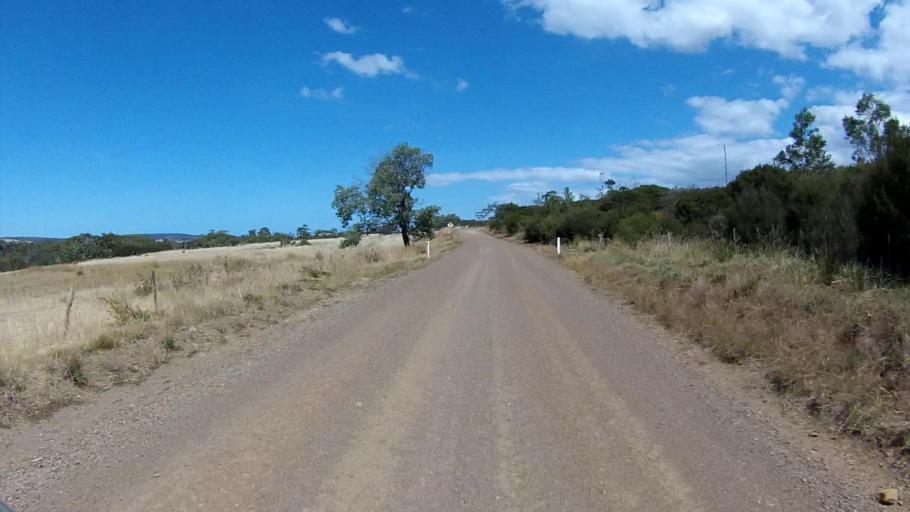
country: AU
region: Tasmania
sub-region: Break O'Day
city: St Helens
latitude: -41.9690
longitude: 148.0736
